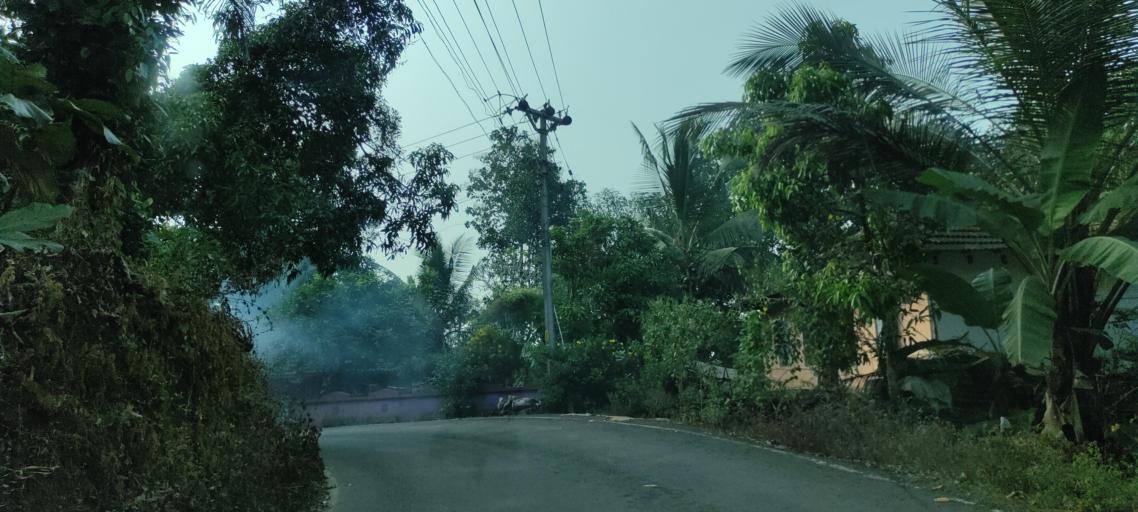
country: IN
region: Kerala
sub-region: Ernakulam
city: Piravam
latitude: 9.8037
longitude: 76.5119
